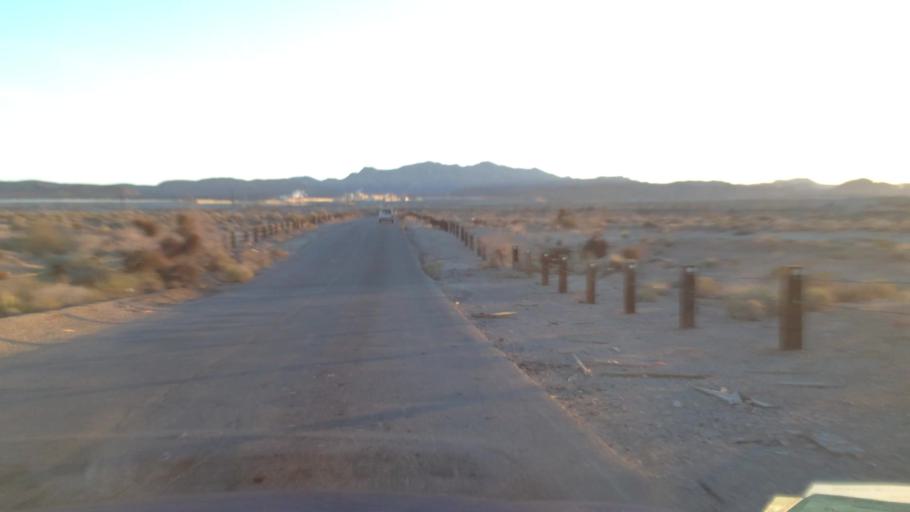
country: US
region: Nevada
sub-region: Clark County
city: Nellis Air Force Base
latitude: 36.2141
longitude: -114.8996
